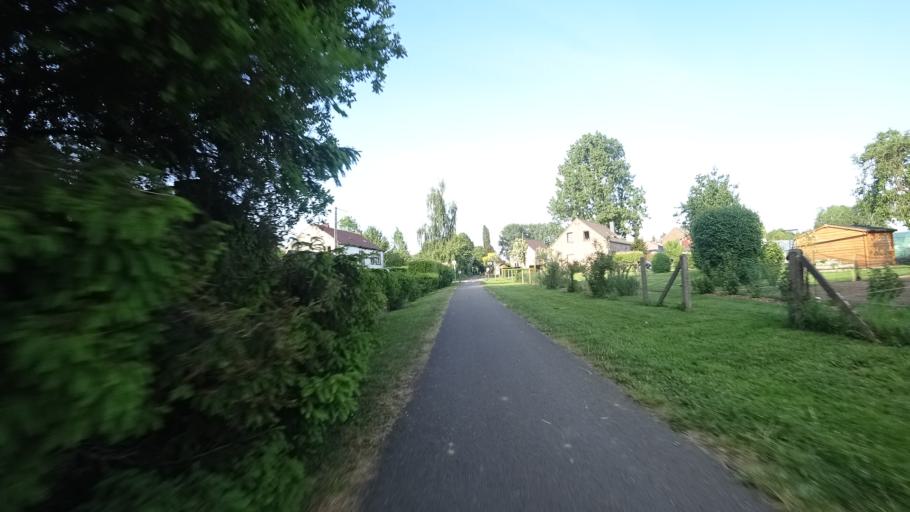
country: BE
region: Wallonia
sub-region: Province de Namur
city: Namur
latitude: 50.5180
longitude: 4.8831
